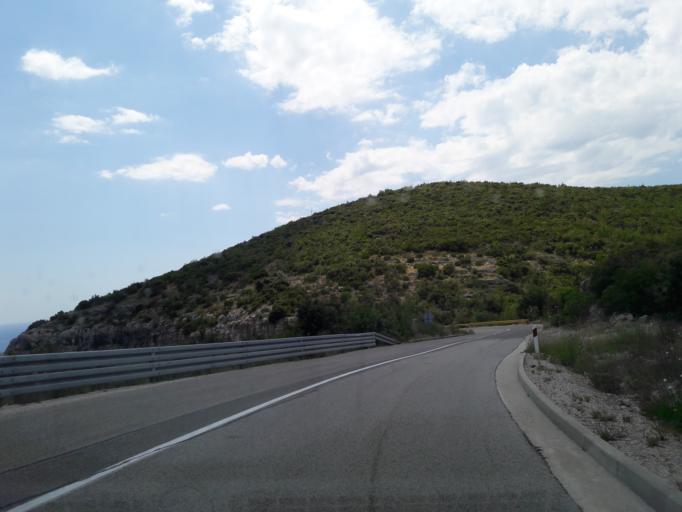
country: HR
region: Dubrovacko-Neretvanska
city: Orebic
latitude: 42.9714
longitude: 17.2607
